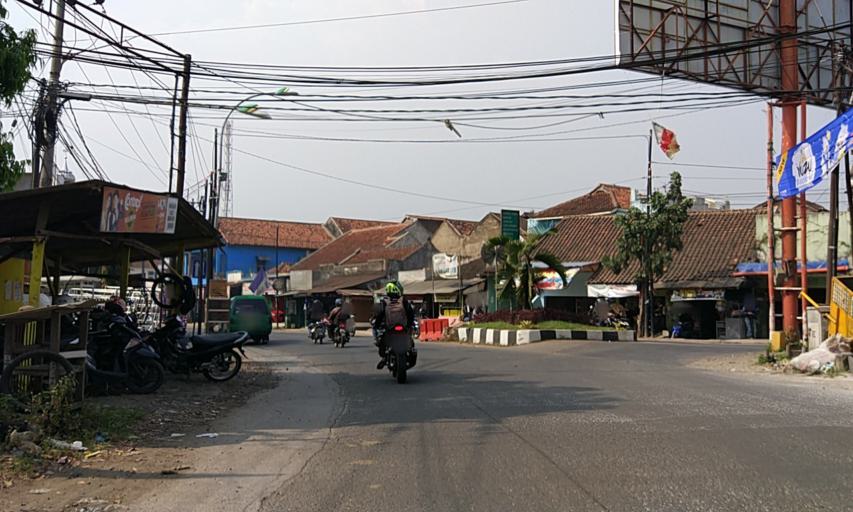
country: ID
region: West Java
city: Soreang
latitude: -7.0164
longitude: 107.5482
